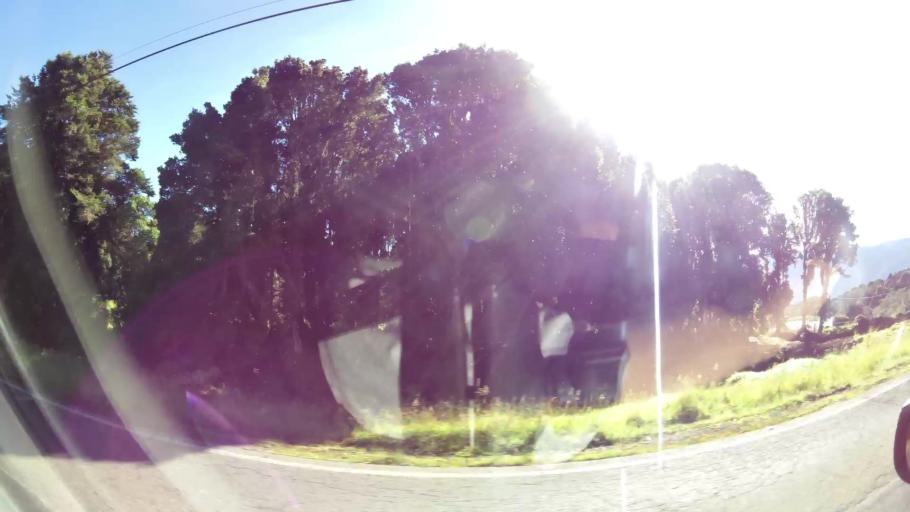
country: CR
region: San Jose
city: San Marcos
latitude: 9.6869
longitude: -83.9213
